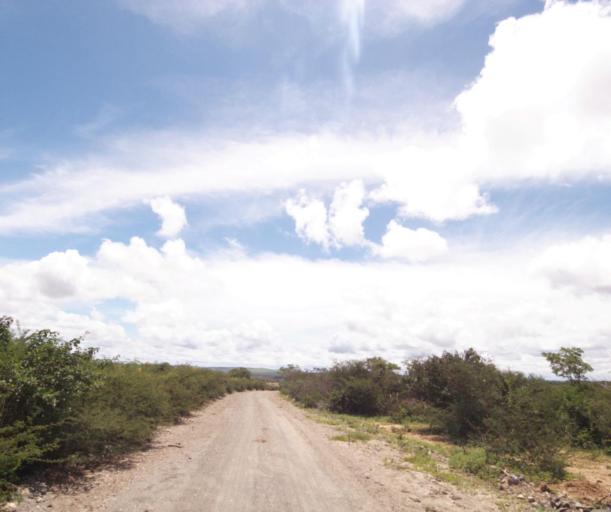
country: BR
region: Bahia
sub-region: Tanhacu
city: Tanhacu
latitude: -14.1919
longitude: -41.0375
